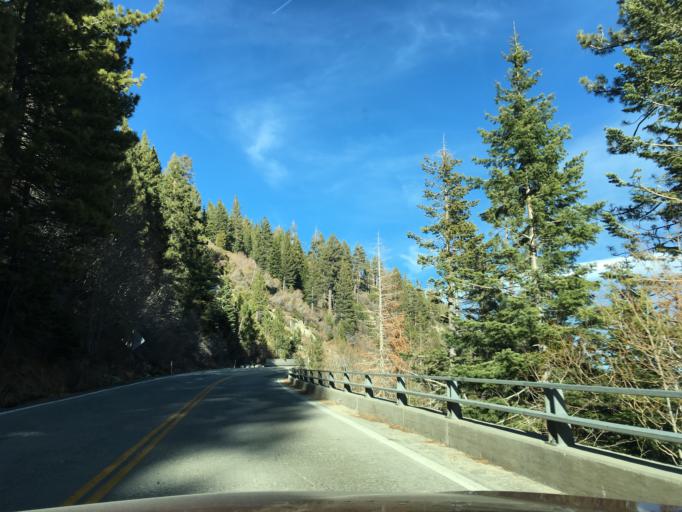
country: US
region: California
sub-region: Placer County
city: Tahoma
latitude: 38.9554
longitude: -120.1099
